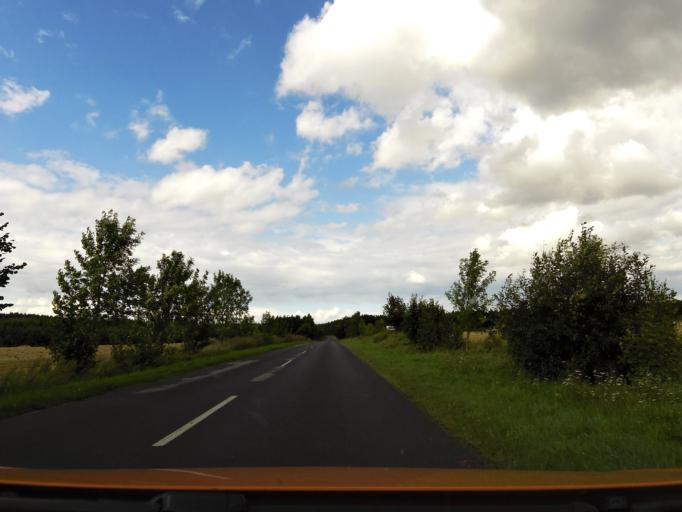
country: PL
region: West Pomeranian Voivodeship
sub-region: Powiat kolobrzeski
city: Kolobrzeg
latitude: 54.0969
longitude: 15.5779
